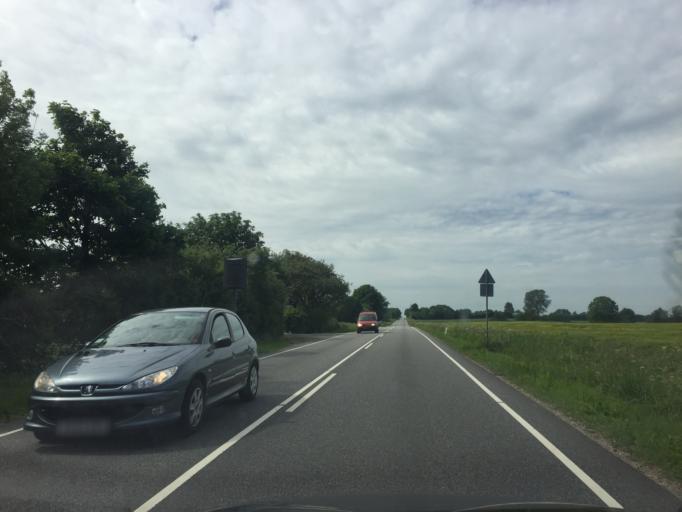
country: DK
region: South Denmark
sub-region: Faaborg-Midtfyn Kommune
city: Ringe
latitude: 55.2132
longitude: 10.5750
